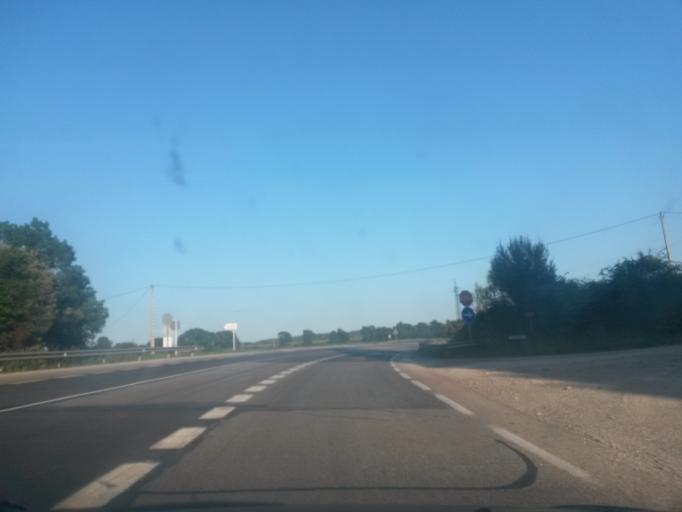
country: ES
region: Catalonia
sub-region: Provincia de Girona
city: Besalu
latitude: 42.1815
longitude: 2.7426
